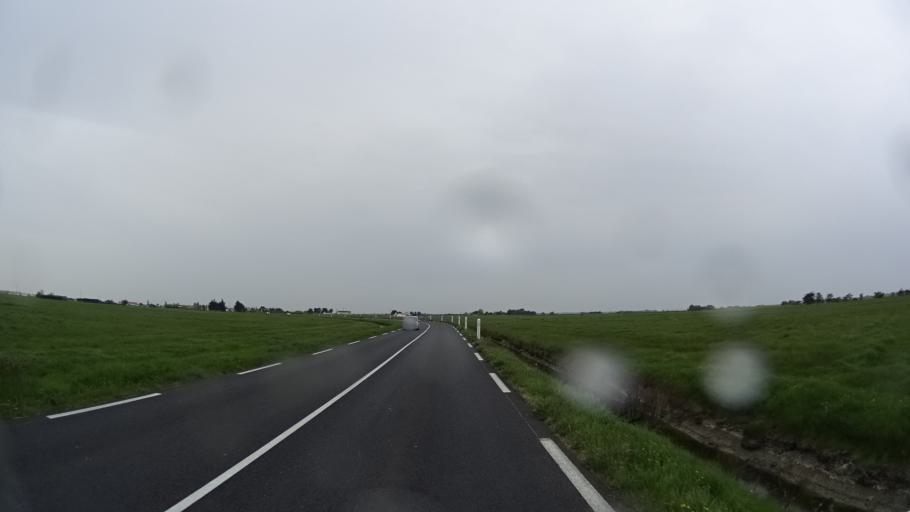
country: FR
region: Pays de la Loire
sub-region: Departement de la Vendee
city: Beauvoir-sur-Mer
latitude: 46.9007
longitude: -2.0612
